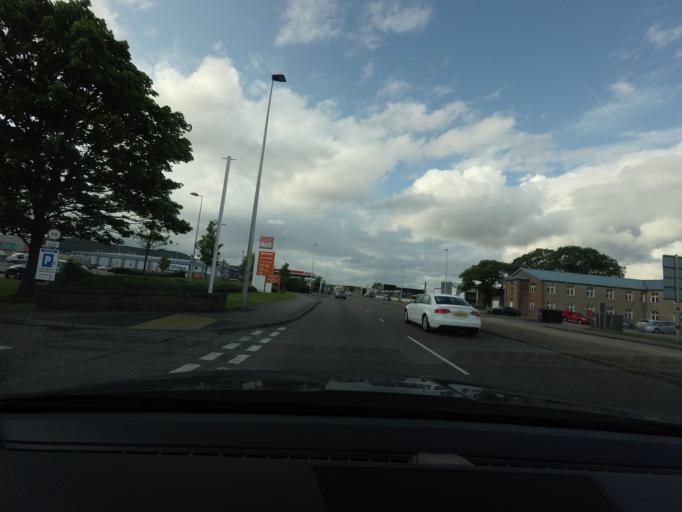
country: GB
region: Scotland
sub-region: Highland
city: Inverness
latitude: 57.4866
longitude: -4.2204
